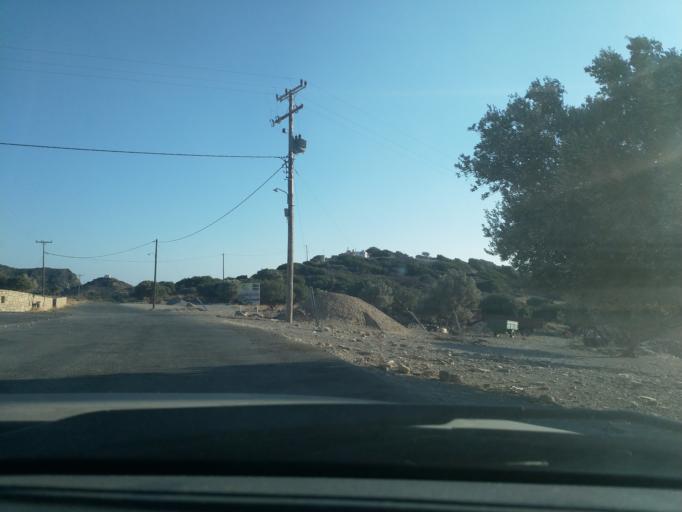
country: GR
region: Crete
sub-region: Nomos Rethymnis
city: Agia Galini
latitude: 35.1221
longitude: 24.5585
